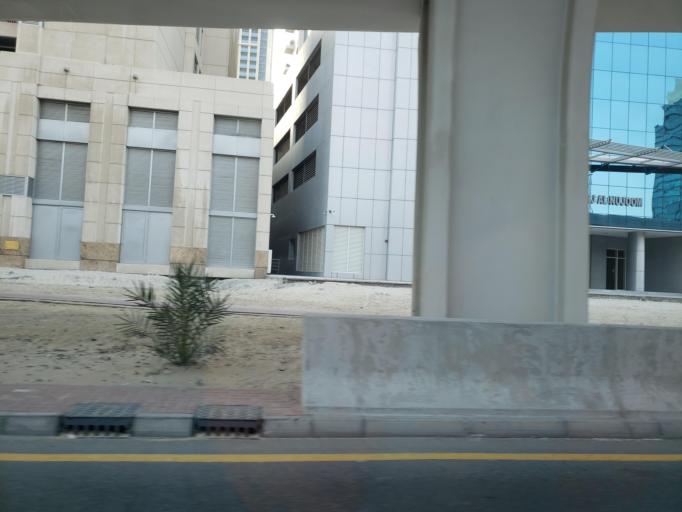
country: AE
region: Dubai
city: Dubai
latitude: 25.1909
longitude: 55.2823
